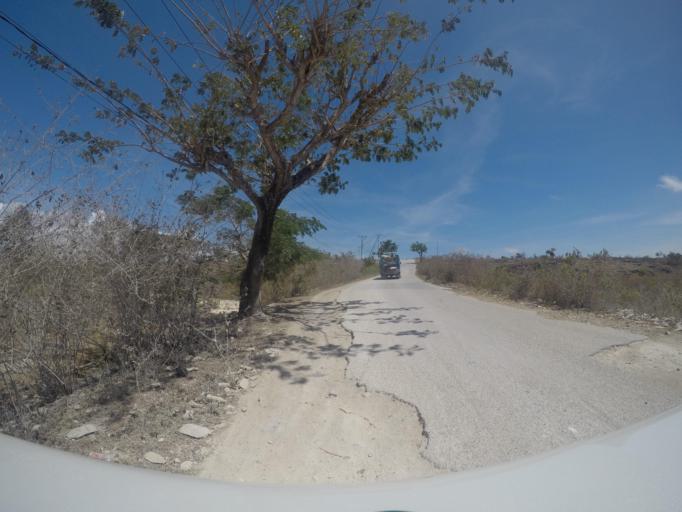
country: TL
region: Baucau
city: Baucau
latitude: -8.4717
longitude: 126.4399
